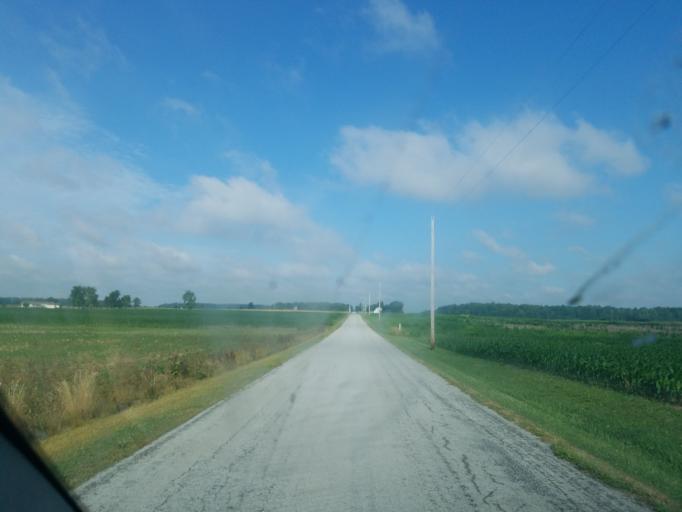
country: US
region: Ohio
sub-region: Hardin County
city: Kenton
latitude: 40.7180
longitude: -83.6860
